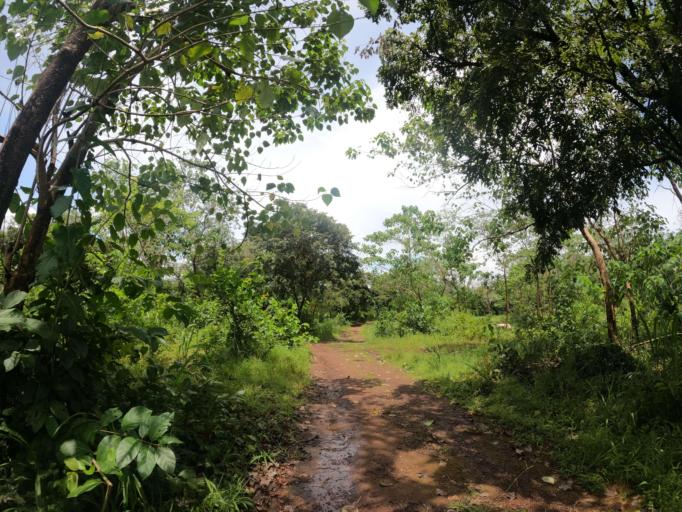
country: SL
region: Northern Province
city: Binkolo
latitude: 9.1551
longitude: -12.1988
